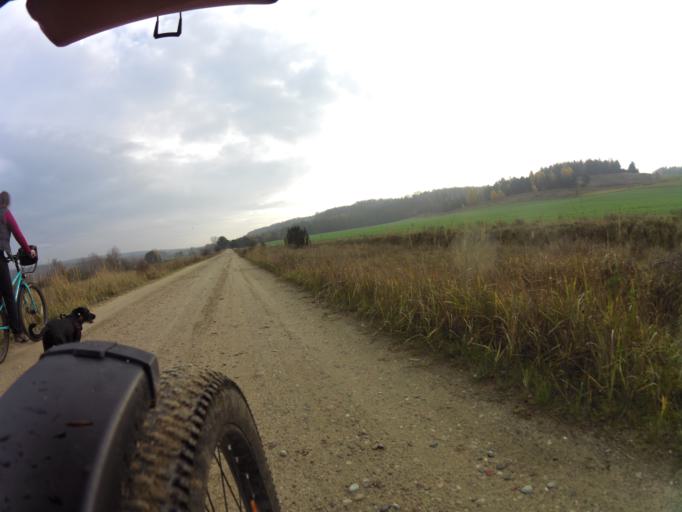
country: PL
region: Pomeranian Voivodeship
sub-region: Powiat wejherowski
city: Gniewino
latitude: 54.7077
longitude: 18.1010
